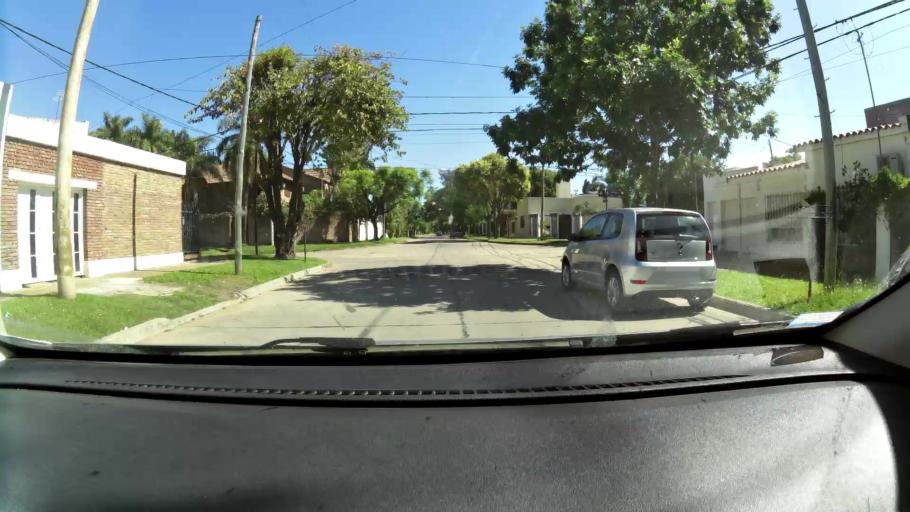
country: AR
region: Santa Fe
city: Santa Fe de la Vera Cruz
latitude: -31.6003
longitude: -60.6691
